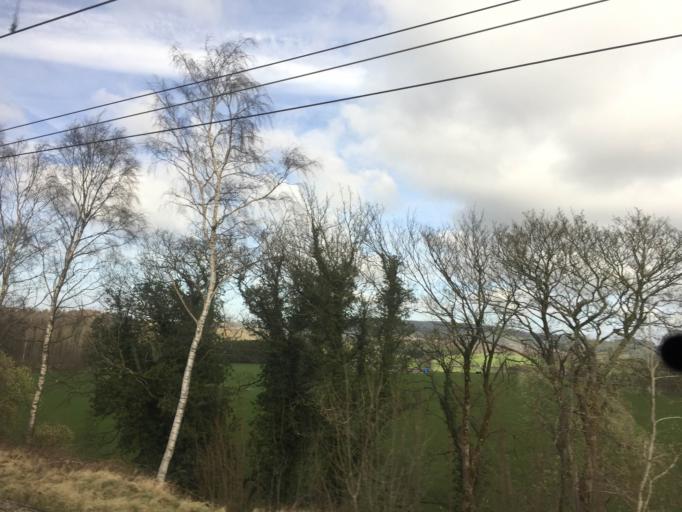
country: GB
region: England
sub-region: Cumbria
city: Penrith
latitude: 54.6354
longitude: -2.7310
